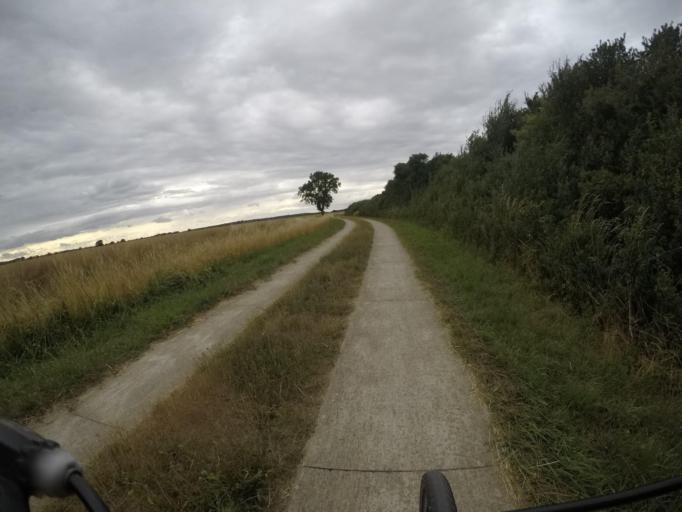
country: DE
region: Lower Saxony
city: Neu Darchau
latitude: 53.2498
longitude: 10.9170
